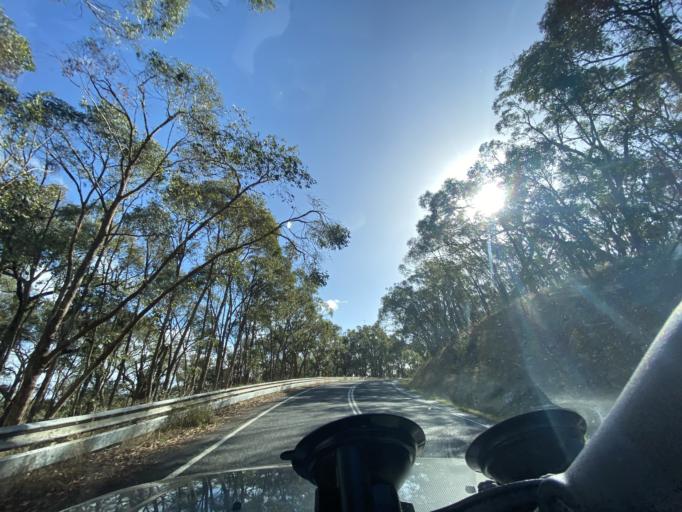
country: AU
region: Victoria
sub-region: Murrindindi
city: Kinglake West
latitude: -37.3020
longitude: 145.3713
